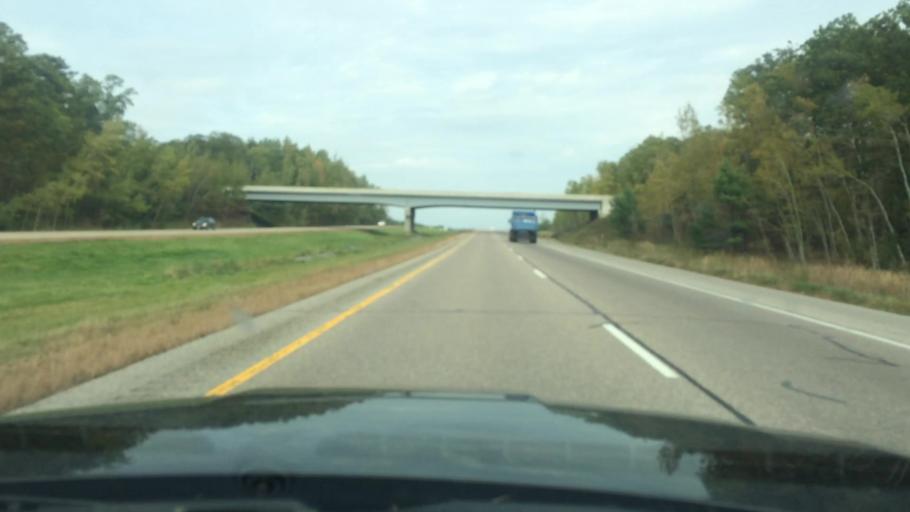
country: US
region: Wisconsin
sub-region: Marathon County
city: Mosinee
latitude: 44.6742
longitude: -89.6419
